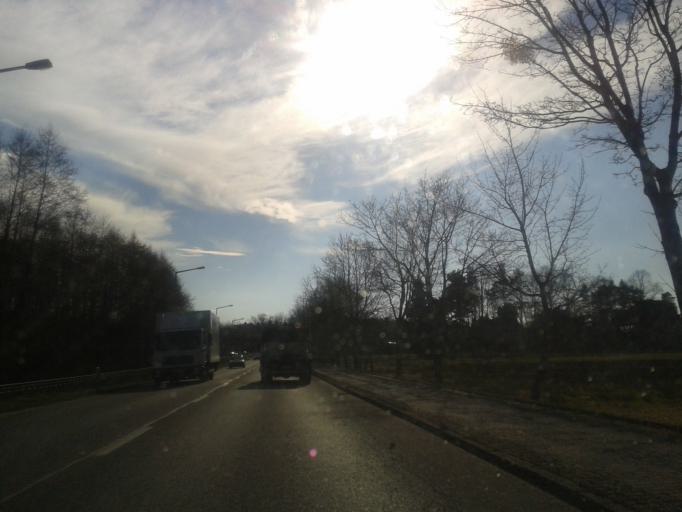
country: DE
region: Saxony
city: Ottendorf-Okrilla
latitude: 51.1375
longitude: 13.7981
